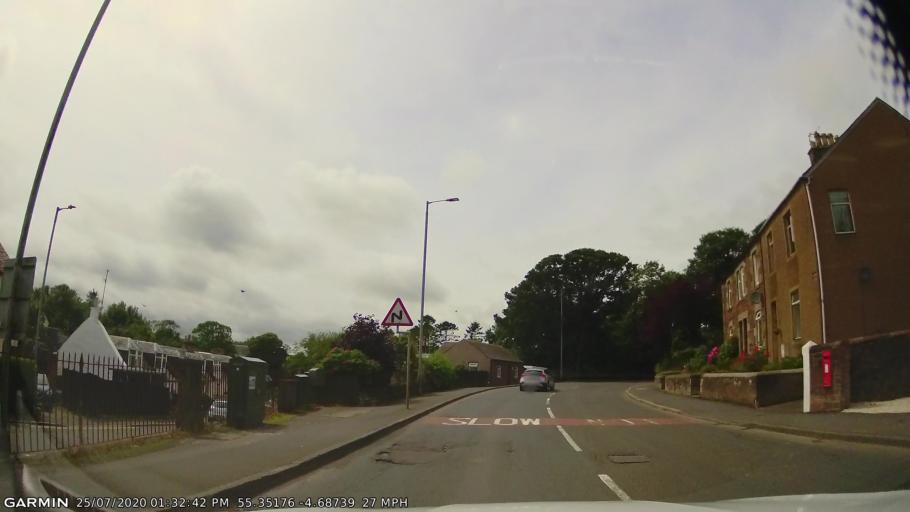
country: GB
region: Scotland
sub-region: South Ayrshire
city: Maybole
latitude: 55.3518
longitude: -4.6874
